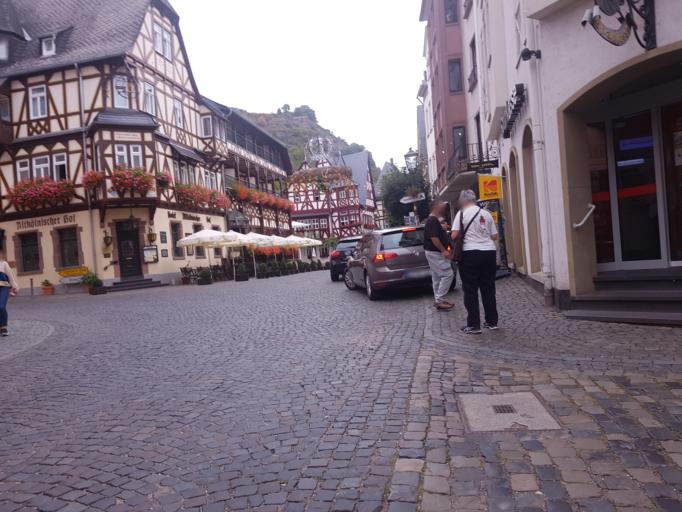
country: DE
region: Rheinland-Pfalz
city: Bacharach
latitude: 50.0598
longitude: 7.7682
